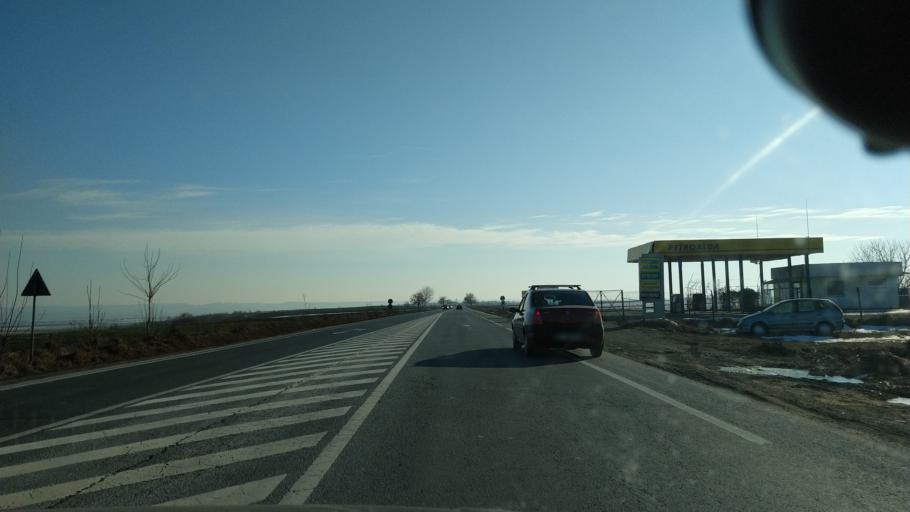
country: RO
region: Iasi
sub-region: Comuna Rachiteni
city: Izvoarele
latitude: 47.0195
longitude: 26.8871
